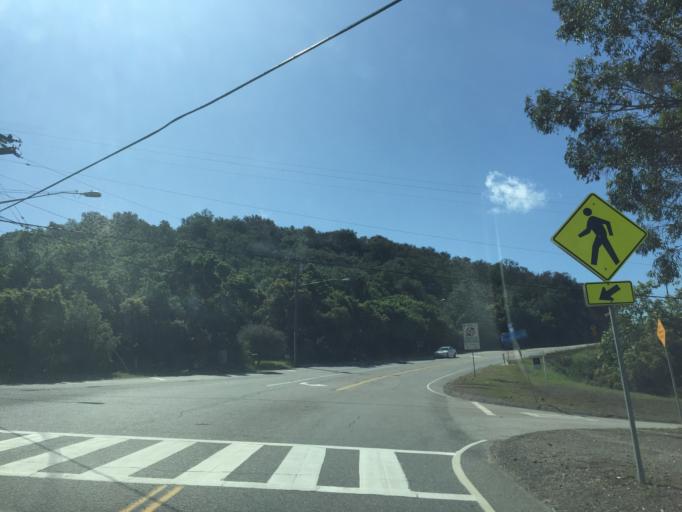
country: US
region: California
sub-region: Los Angeles County
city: Westlake Village
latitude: 34.0898
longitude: -118.8155
